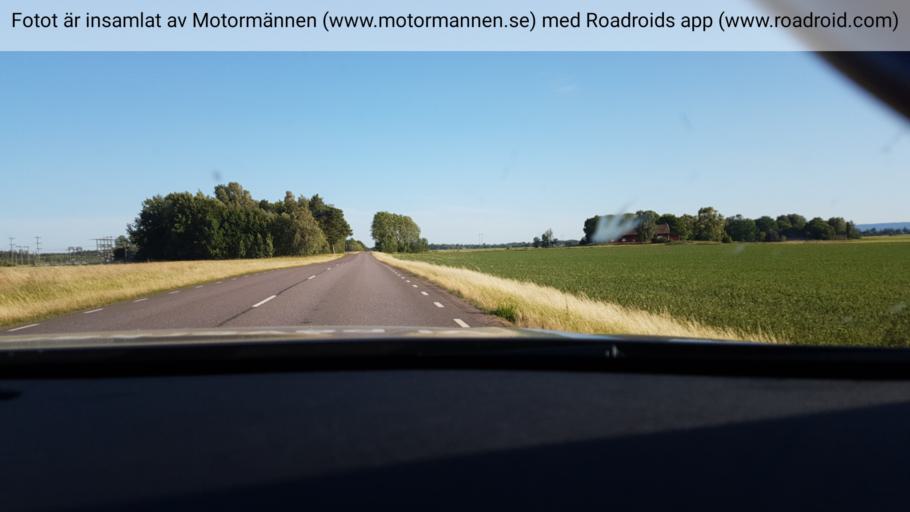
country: SE
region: Vaestra Goetaland
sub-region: Toreboda Kommun
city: Toereboda
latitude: 58.6028
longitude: 14.0094
